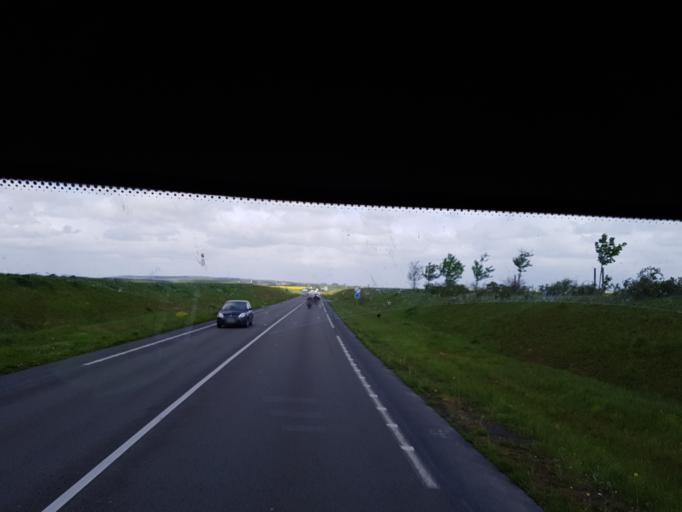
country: FR
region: Nord-Pas-de-Calais
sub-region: Departement du Nord
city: Proville
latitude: 50.1434
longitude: 3.2104
